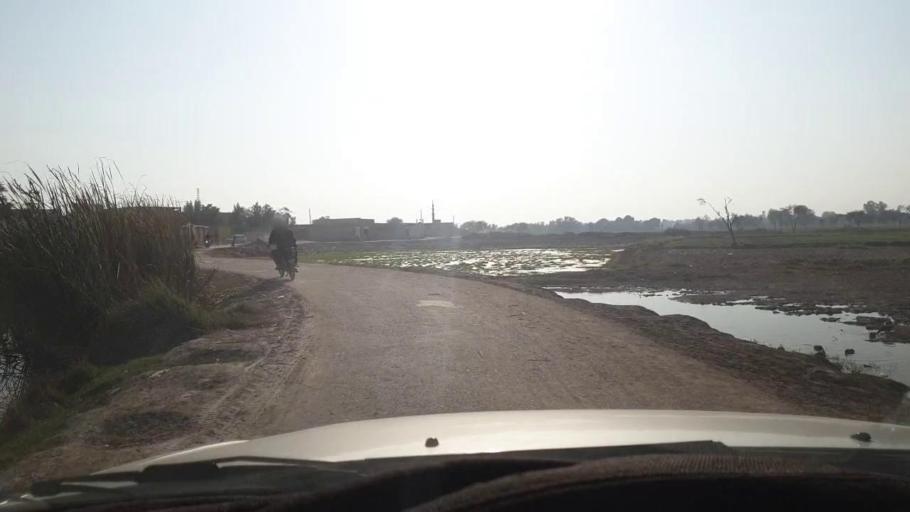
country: PK
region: Sindh
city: Mirpur Mathelo
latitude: 28.0213
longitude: 69.6053
